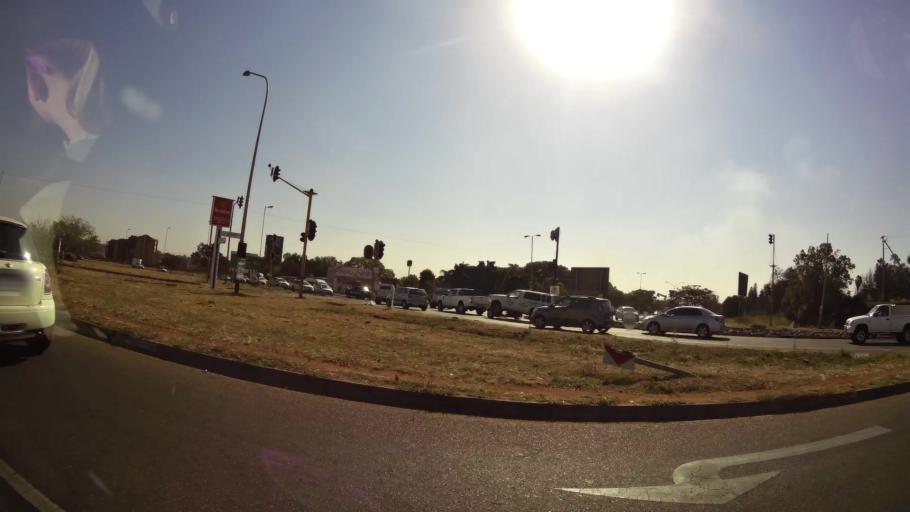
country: ZA
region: Gauteng
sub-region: City of Tshwane Metropolitan Municipality
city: Pretoria
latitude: -25.6770
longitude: 28.1951
